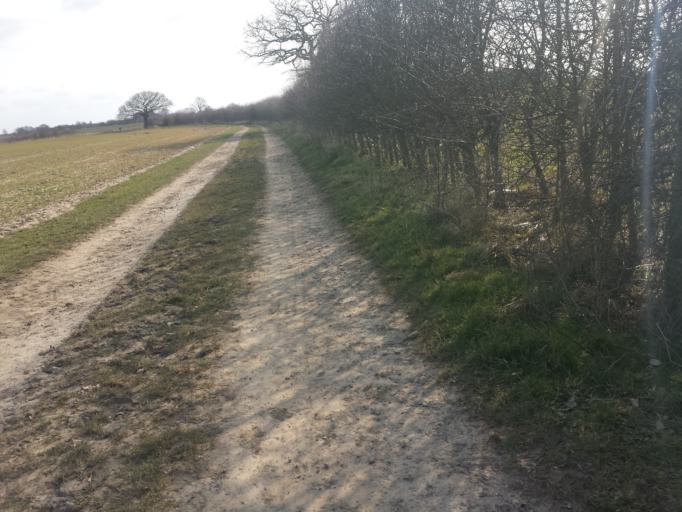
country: GB
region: England
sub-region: Essex
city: Little Clacton
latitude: 51.8960
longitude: 1.1616
